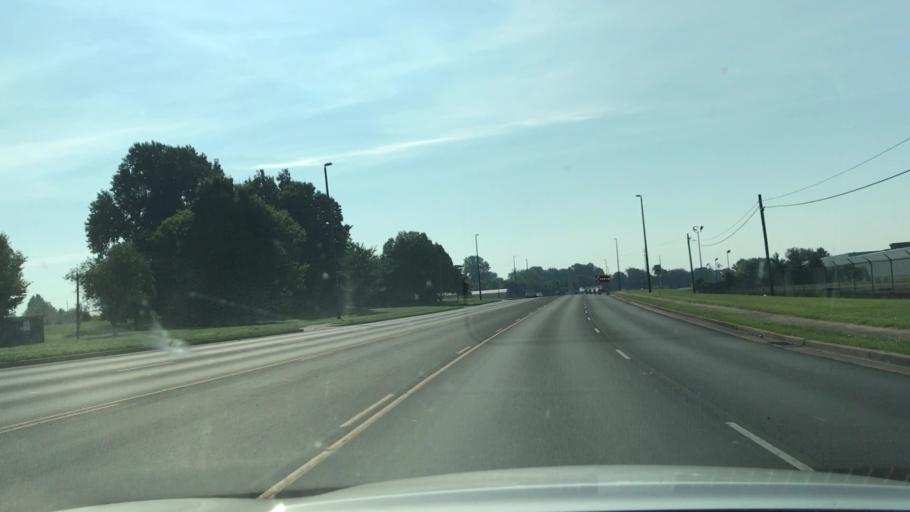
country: US
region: Kentucky
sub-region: Barren County
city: Glasgow
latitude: 37.0097
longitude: -85.9408
